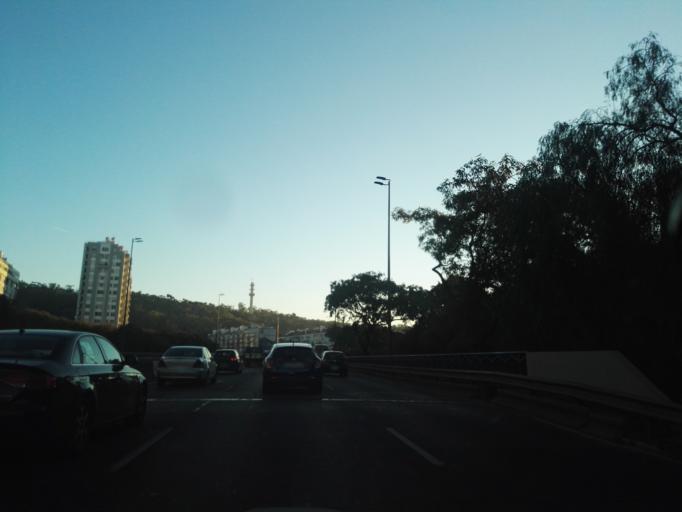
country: PT
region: Lisbon
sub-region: Odivelas
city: Pontinha
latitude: 38.7487
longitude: -9.1895
